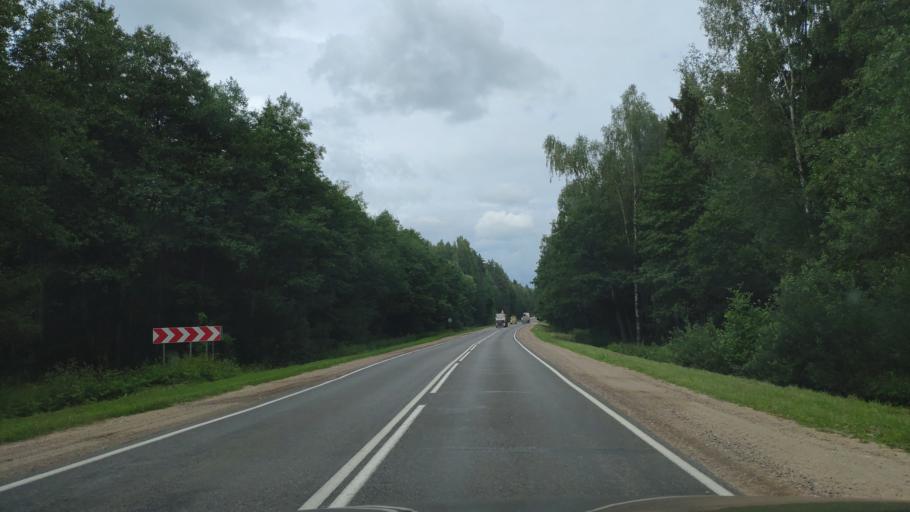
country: BY
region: Minsk
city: Novosel'ye
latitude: 53.9310
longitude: 27.2434
